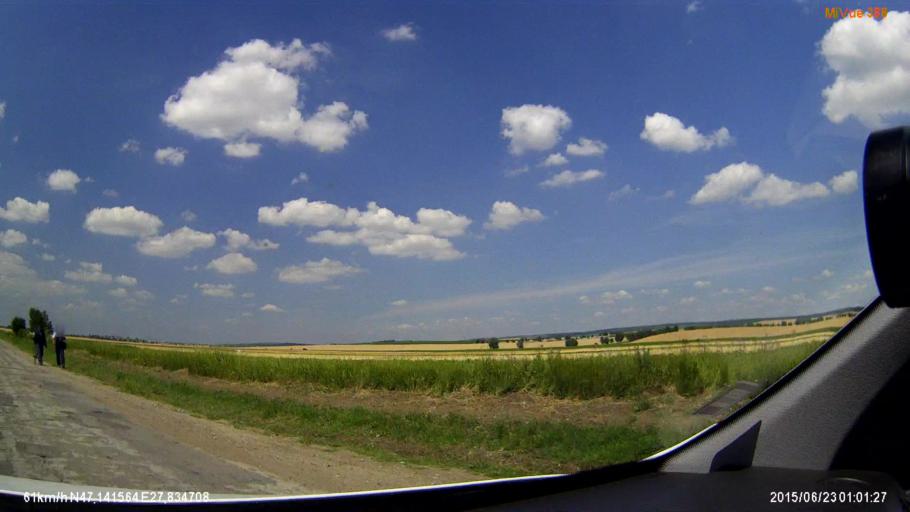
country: RO
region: Iasi
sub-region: Comuna Tutora
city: Tutora
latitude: 47.1414
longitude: 27.8349
